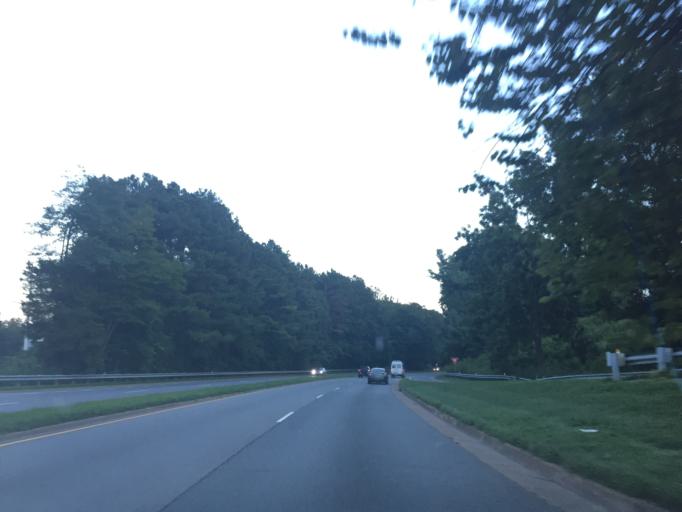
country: US
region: Virginia
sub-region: City of Charlottesville
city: Charlottesville
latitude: 38.0549
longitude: -78.4832
